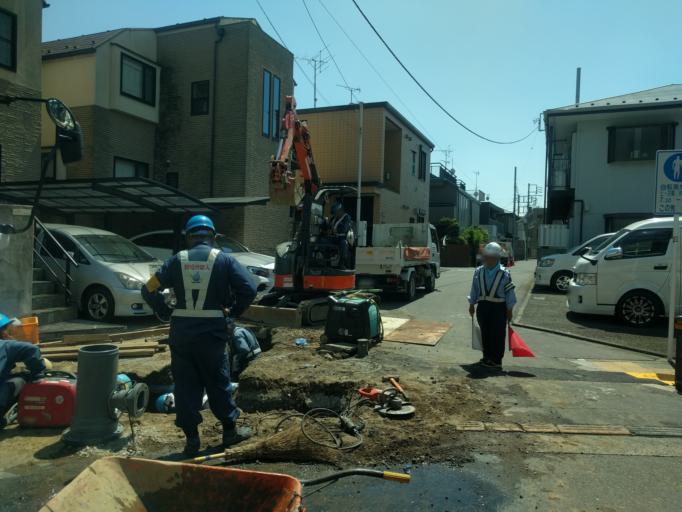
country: JP
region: Tokyo
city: Mitaka-shi
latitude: 35.6631
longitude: 139.6220
